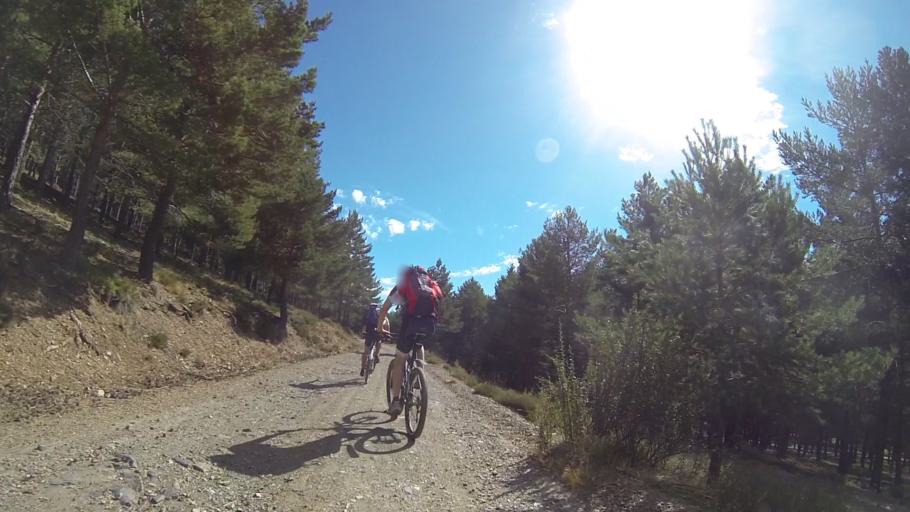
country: ES
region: Andalusia
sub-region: Provincia de Granada
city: Ferreira
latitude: 37.1119
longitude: -3.0270
